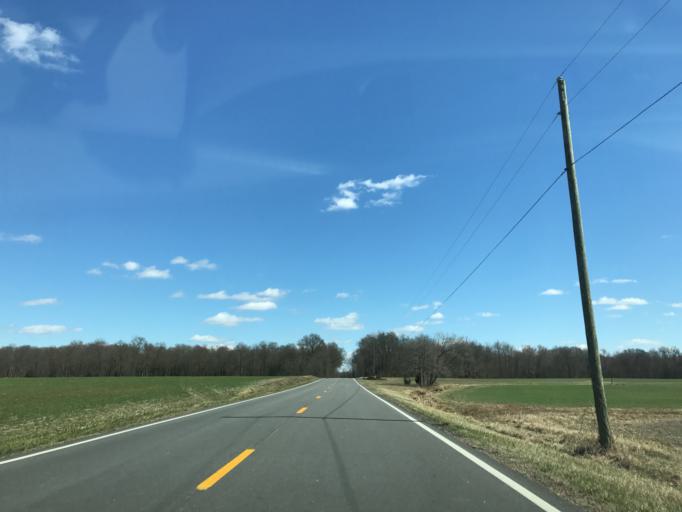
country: US
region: Delaware
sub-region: Kent County
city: Clayton
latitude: 39.2532
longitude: -75.8006
